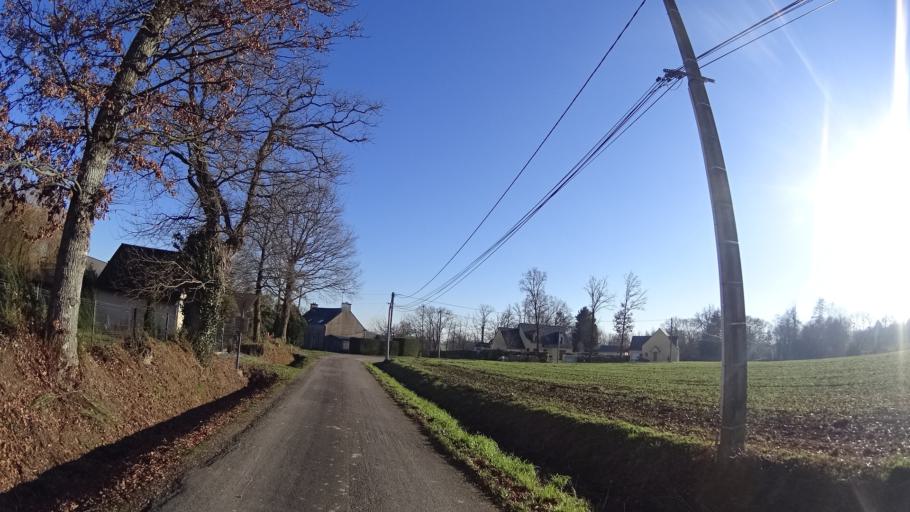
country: FR
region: Brittany
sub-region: Departement du Morbihan
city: Allaire
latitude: 47.6337
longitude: -2.1486
